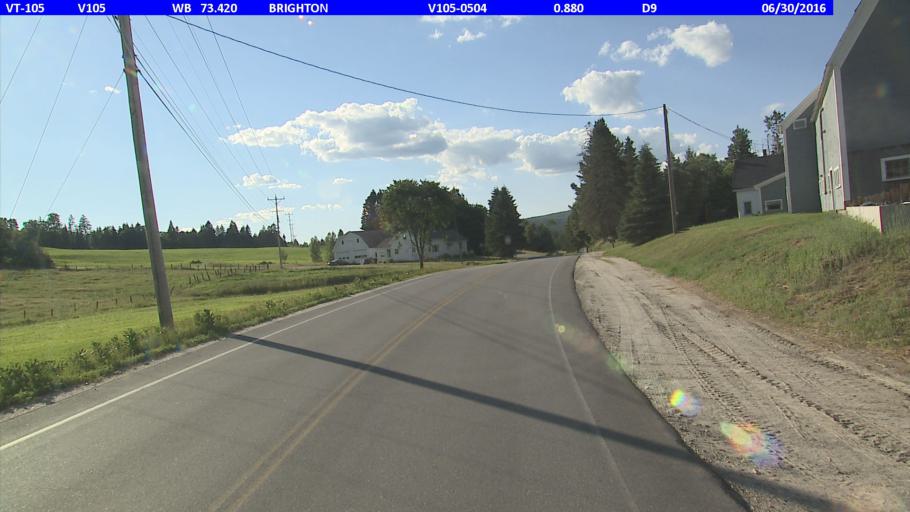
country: US
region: Vermont
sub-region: Caledonia County
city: Lyndonville
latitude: 44.8067
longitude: -71.9319
